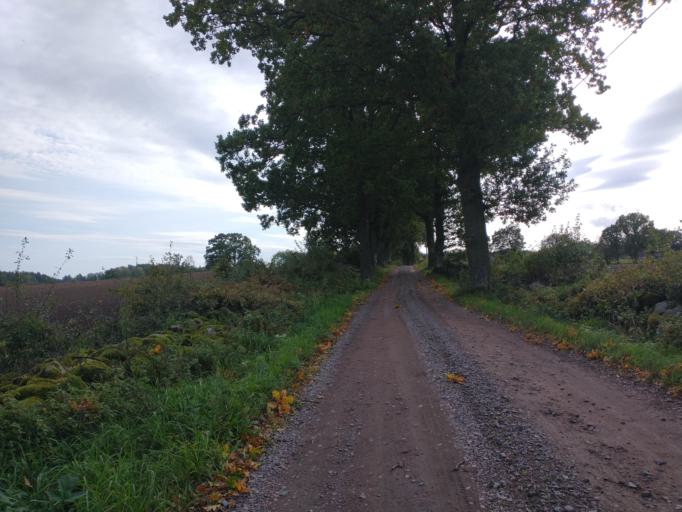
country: SE
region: Kalmar
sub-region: Kalmar Kommun
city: Lindsdal
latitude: 56.7747
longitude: 16.3073
